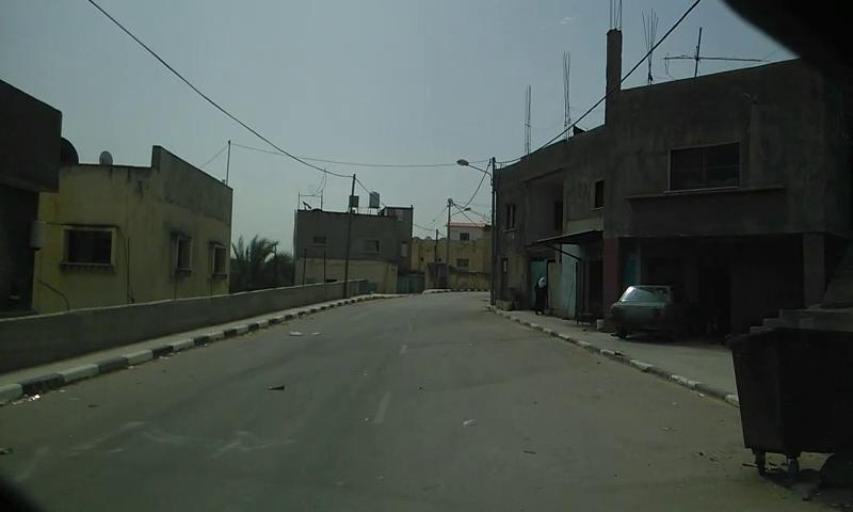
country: PS
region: West Bank
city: Silat al Harithiyah
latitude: 32.5196
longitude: 35.2199
